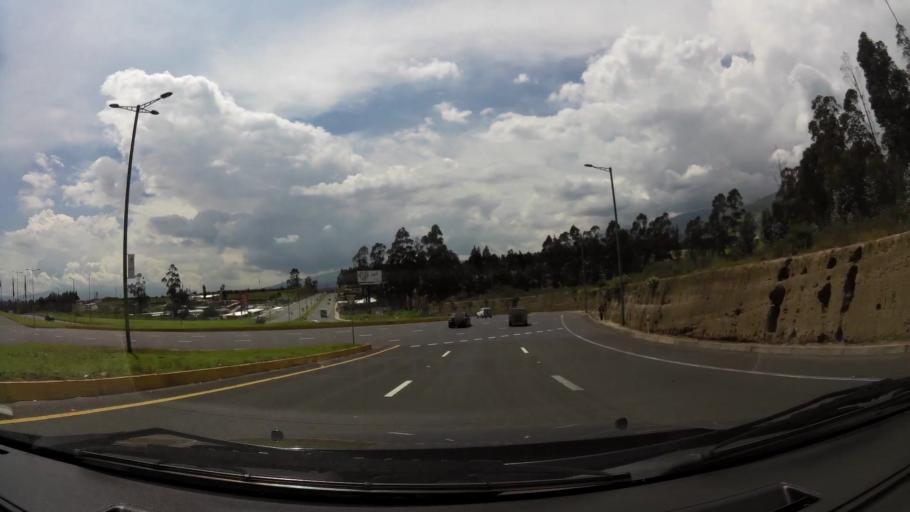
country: EC
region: Pichincha
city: Sangolqui
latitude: -0.1908
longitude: -78.3389
